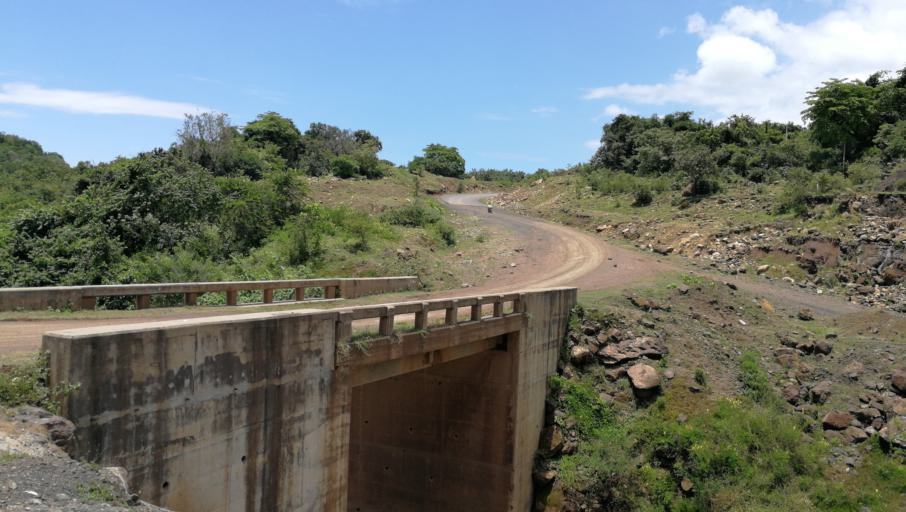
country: ET
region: Southern Nations, Nationalities, and People's Region
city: Areka
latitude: 6.9267
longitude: 37.3014
